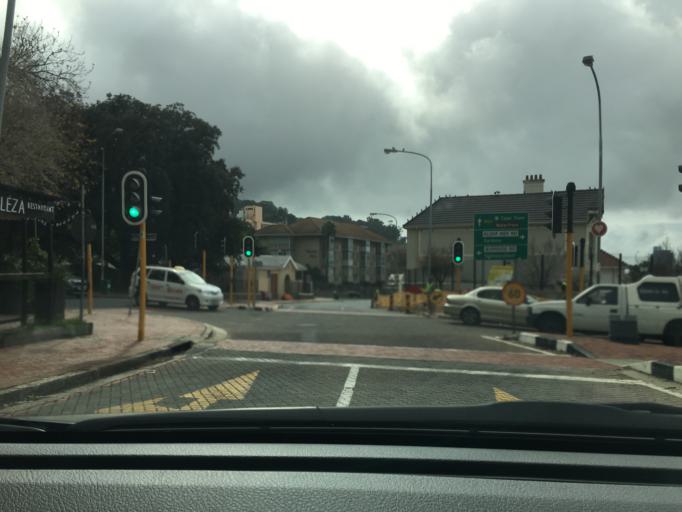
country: ZA
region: Western Cape
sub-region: City of Cape Town
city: Cape Town
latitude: -33.9299
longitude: 18.4078
